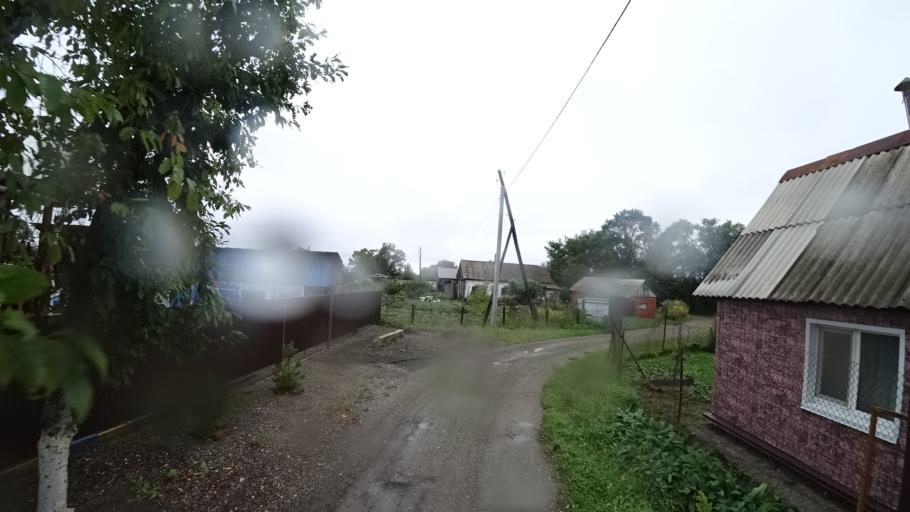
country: RU
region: Primorskiy
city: Monastyrishche
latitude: 44.2049
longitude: 132.4225
